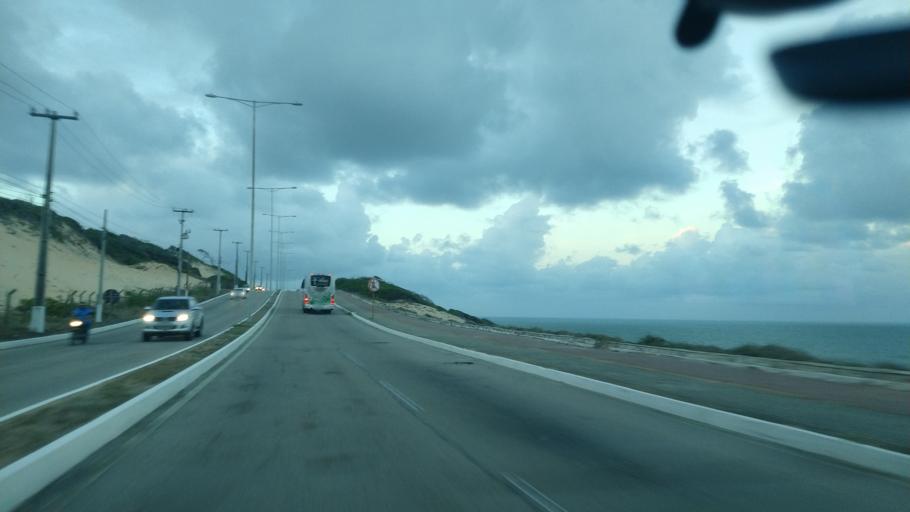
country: BR
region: Rio Grande do Norte
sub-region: Natal
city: Natal
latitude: -5.8223
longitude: -35.1832
